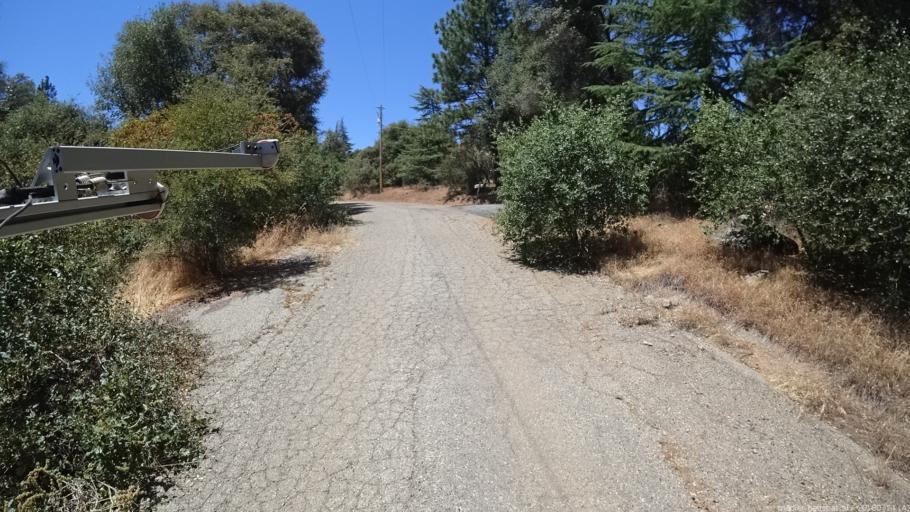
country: US
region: California
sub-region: Madera County
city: Ahwahnee
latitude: 37.4058
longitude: -119.7332
